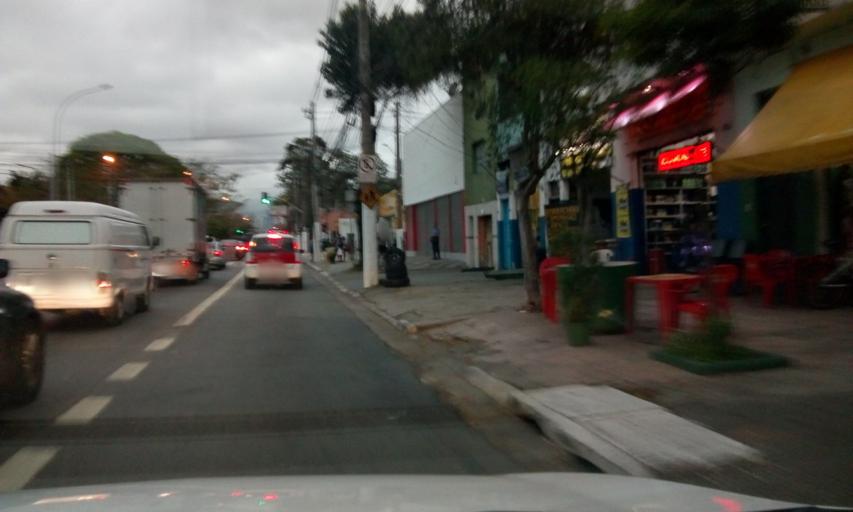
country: BR
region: Sao Paulo
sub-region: Sao Paulo
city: Sao Paulo
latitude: -23.5261
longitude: -46.6253
